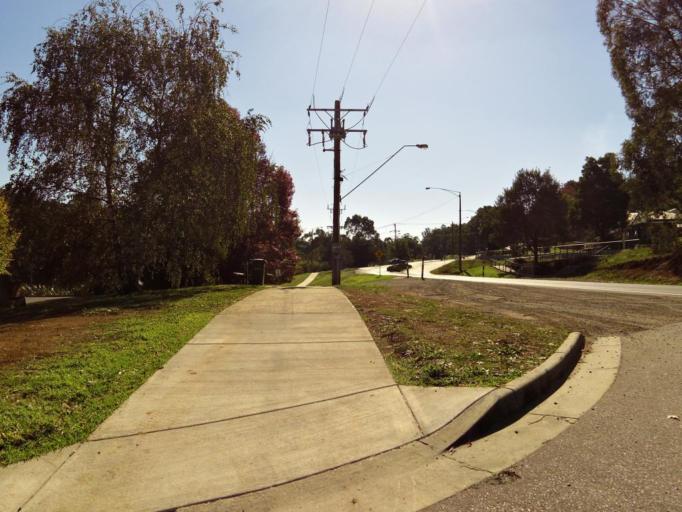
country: AU
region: Victoria
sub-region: Cardinia
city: Cockatoo
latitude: -37.9369
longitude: 145.4914
